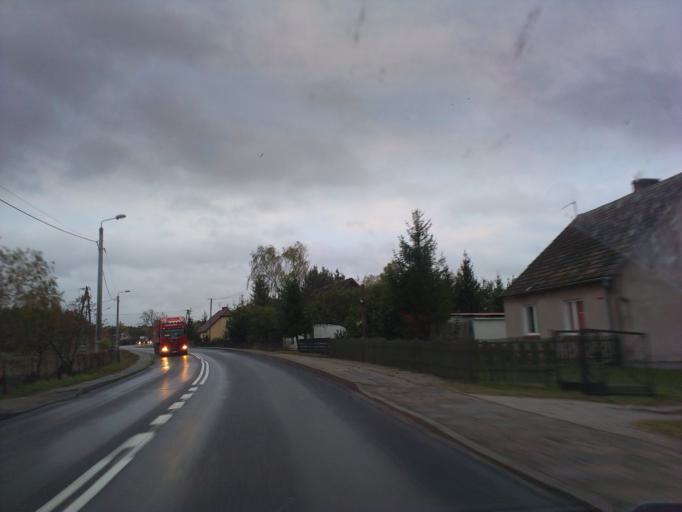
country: PL
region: Kujawsko-Pomorskie
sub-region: Powiat tucholski
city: Cekcyn
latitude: 53.5316
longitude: 17.9448
